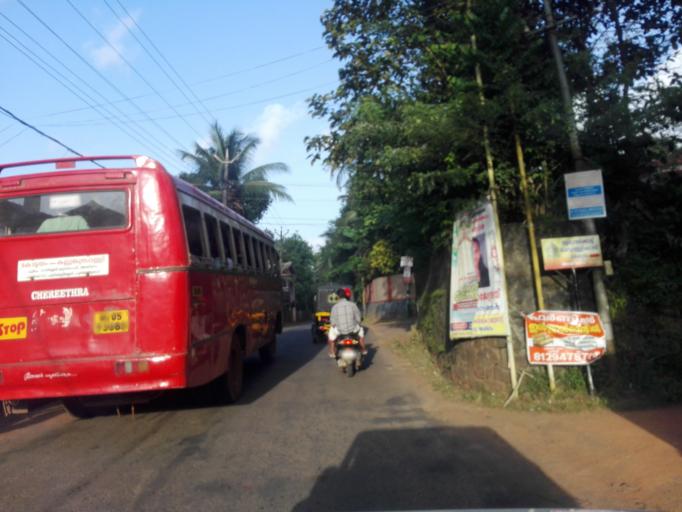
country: IN
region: Kerala
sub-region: Kottayam
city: Kottayam
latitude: 9.6118
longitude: 76.4999
